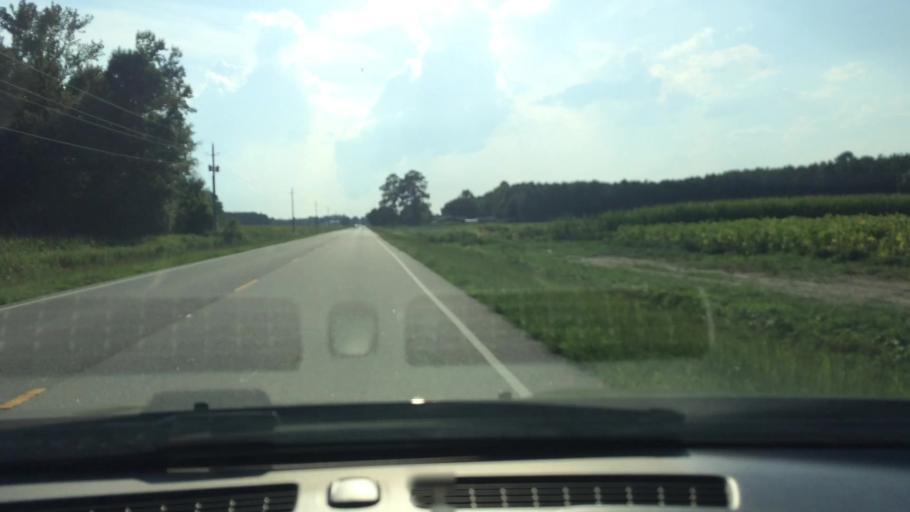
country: US
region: North Carolina
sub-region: Pitt County
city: Ayden
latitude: 35.4708
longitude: -77.3764
